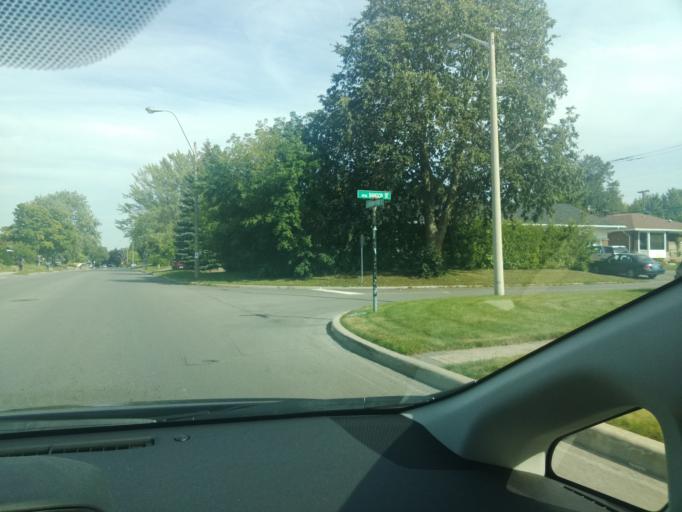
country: CA
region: Ontario
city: Ottawa
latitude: 45.3943
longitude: -75.6305
